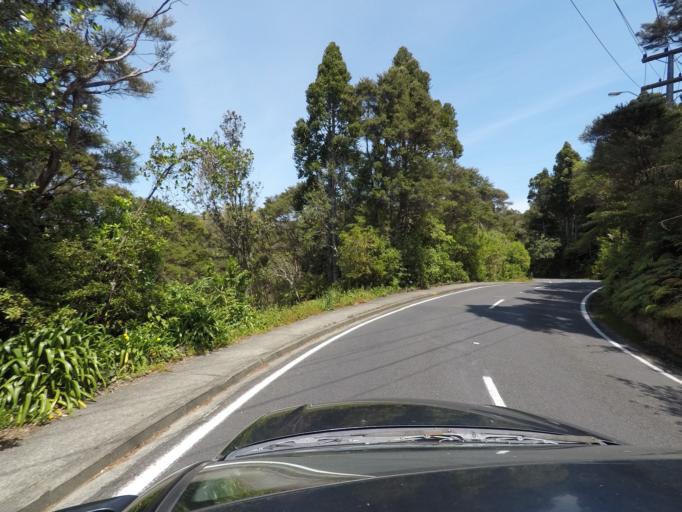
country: NZ
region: Auckland
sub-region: Auckland
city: Titirangi
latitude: -36.9608
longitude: 174.6423
